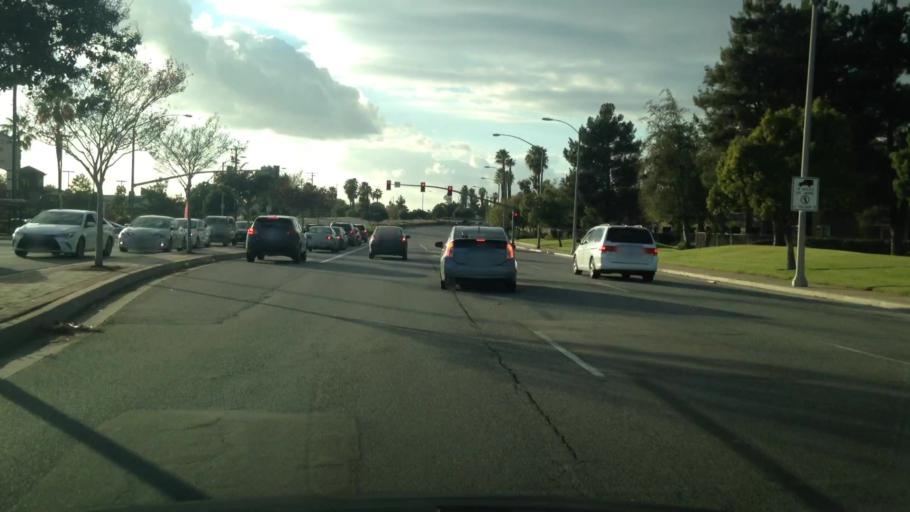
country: US
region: California
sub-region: Riverside County
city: Woodcrest
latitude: 33.9165
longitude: -117.3256
